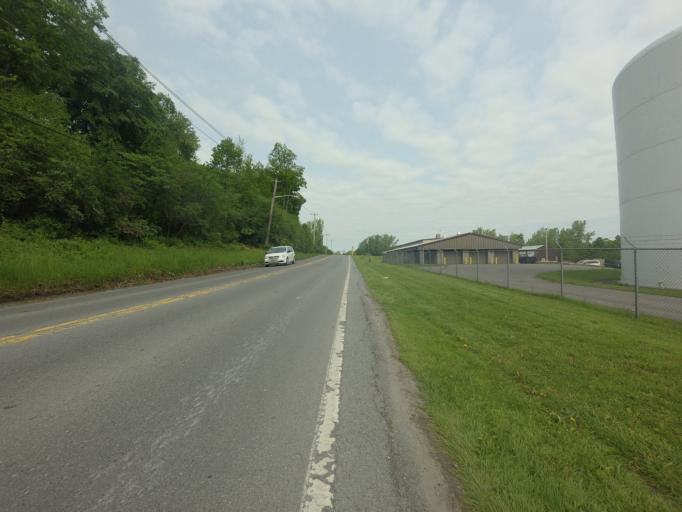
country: US
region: New York
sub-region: Jefferson County
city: Watertown
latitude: 43.9757
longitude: -75.8763
